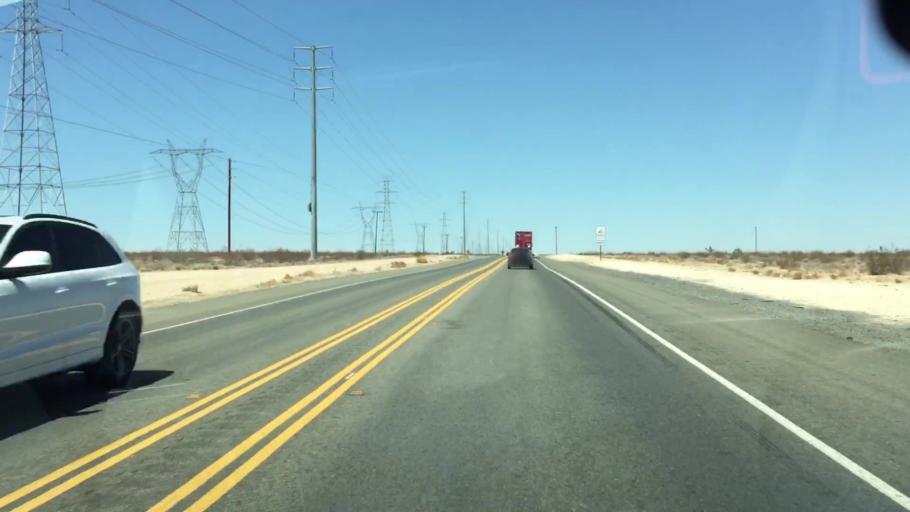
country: US
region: California
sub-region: San Bernardino County
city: Adelanto
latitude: 34.7009
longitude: -117.4536
